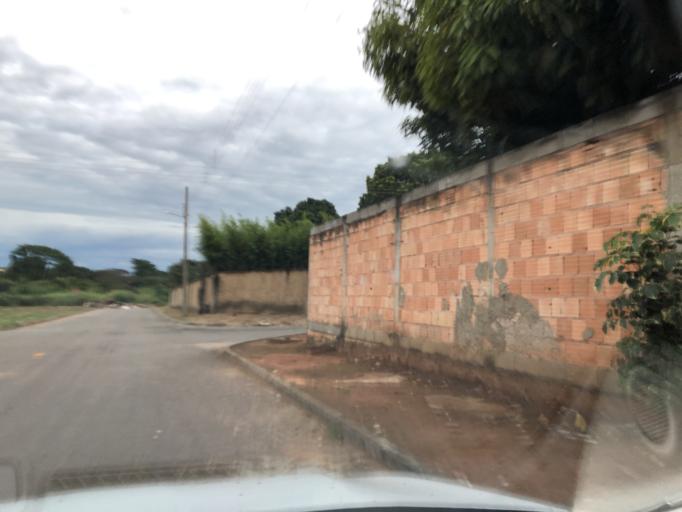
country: BR
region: Goias
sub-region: Luziania
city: Luziania
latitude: -16.1571
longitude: -47.9474
